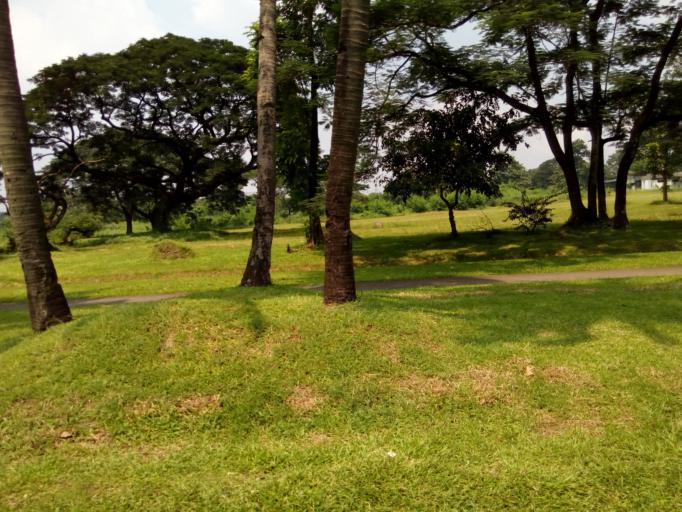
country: PH
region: Metro Manila
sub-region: Quezon City
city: Quezon City
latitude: 14.6550
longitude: 121.0588
